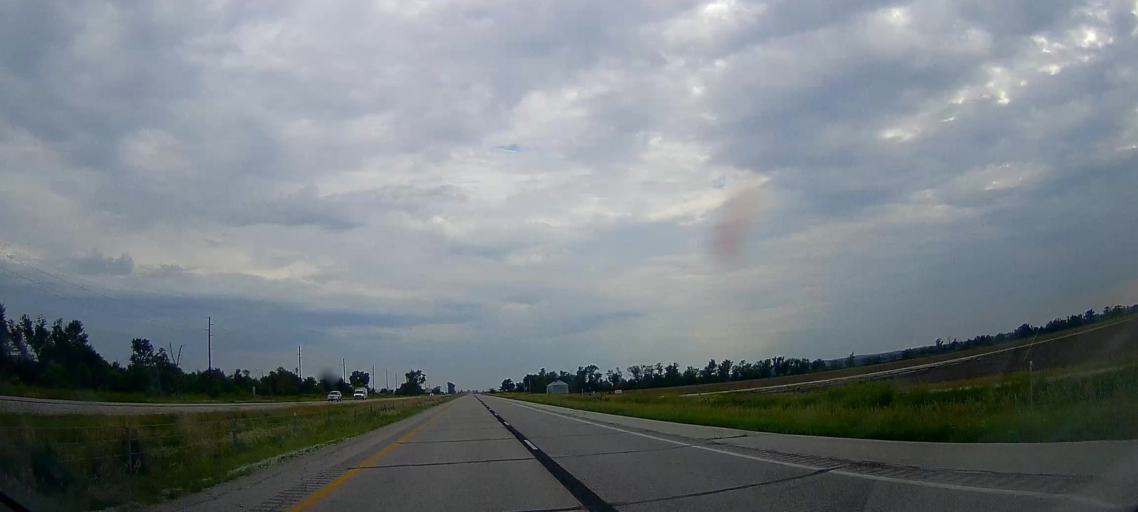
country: US
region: Iowa
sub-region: Harrison County
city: Missouri Valley
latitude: 41.4718
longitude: -95.8997
